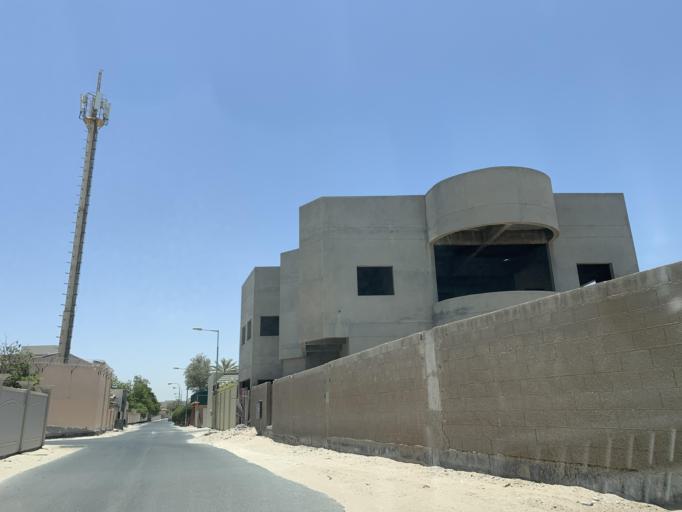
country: BH
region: Manama
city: Jidd Hafs
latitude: 26.2252
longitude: 50.4841
